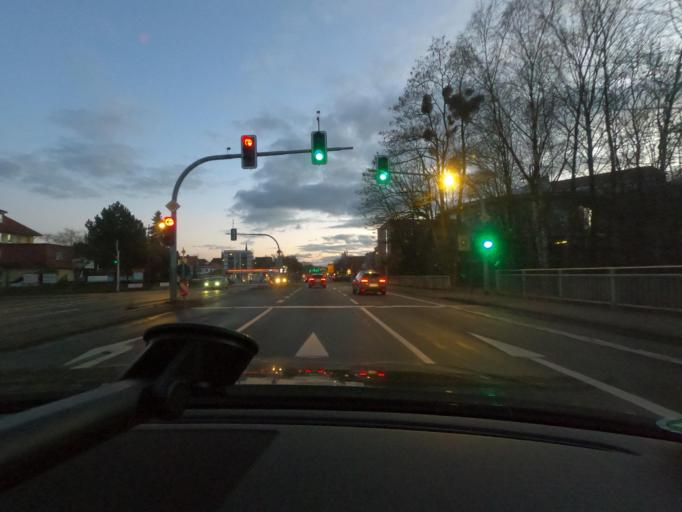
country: DE
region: Lower Saxony
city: Herzberg am Harz
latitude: 51.6578
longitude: 10.3337
